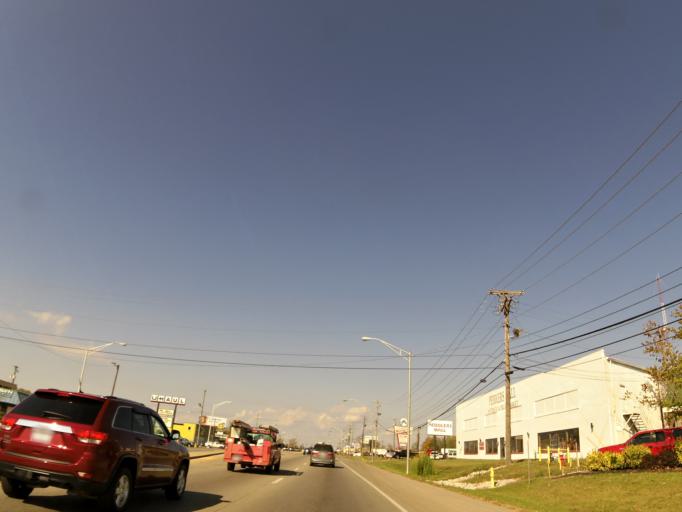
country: US
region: Kentucky
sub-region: Fayette County
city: Lexington-Fayette
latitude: 38.0311
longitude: -84.4526
